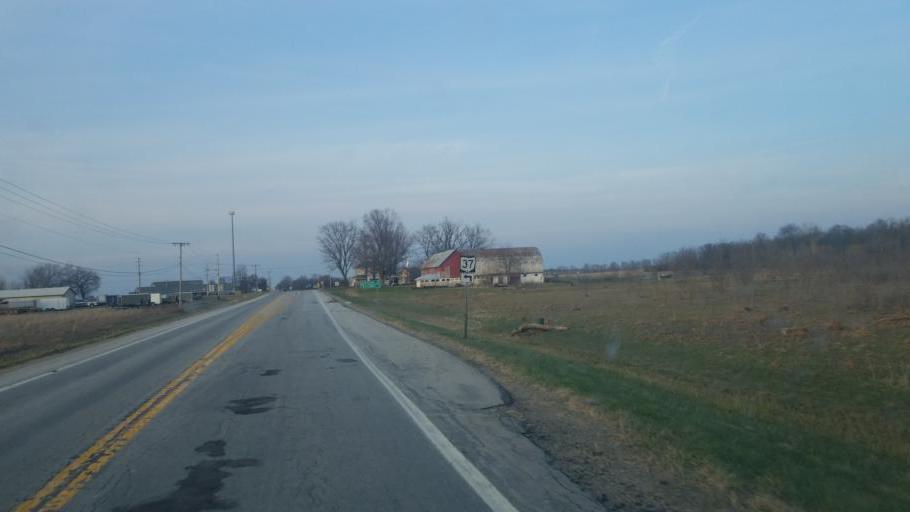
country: US
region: Ohio
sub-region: Union County
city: Richwood
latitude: 40.3928
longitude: -83.2718
